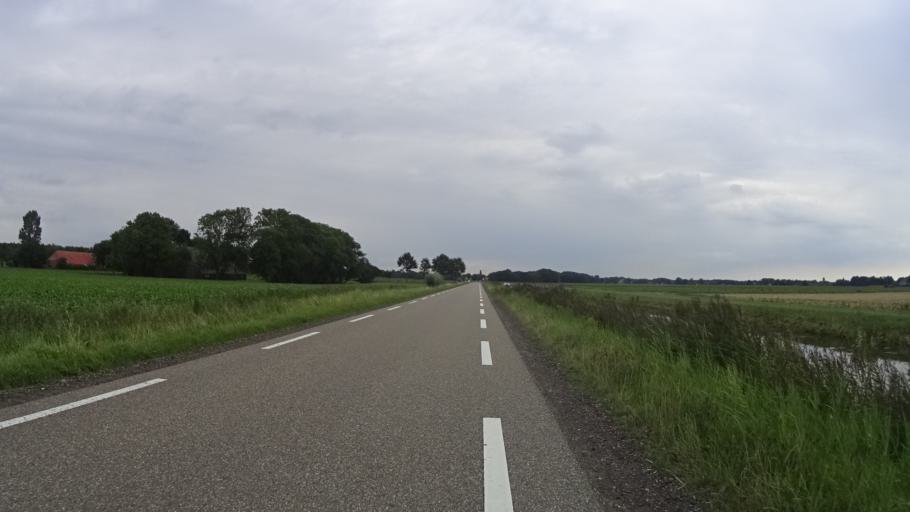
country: NL
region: Groningen
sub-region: Gemeente Slochteren
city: Slochteren
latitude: 53.2268
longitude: 6.7786
